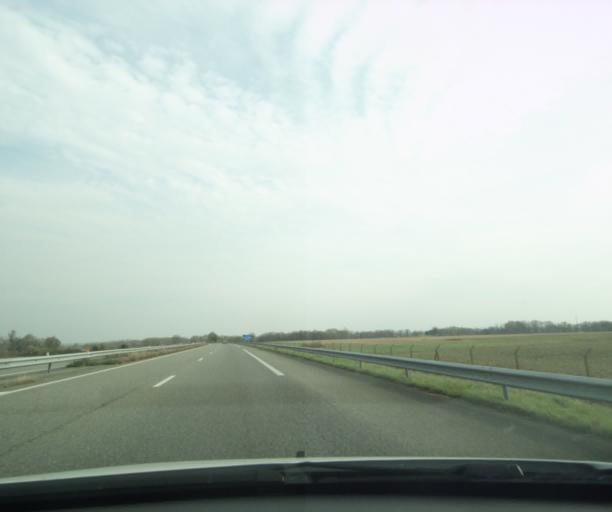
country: FR
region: Aquitaine
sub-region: Departement des Pyrenees-Atlantiques
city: Mont
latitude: 43.4294
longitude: -0.6271
